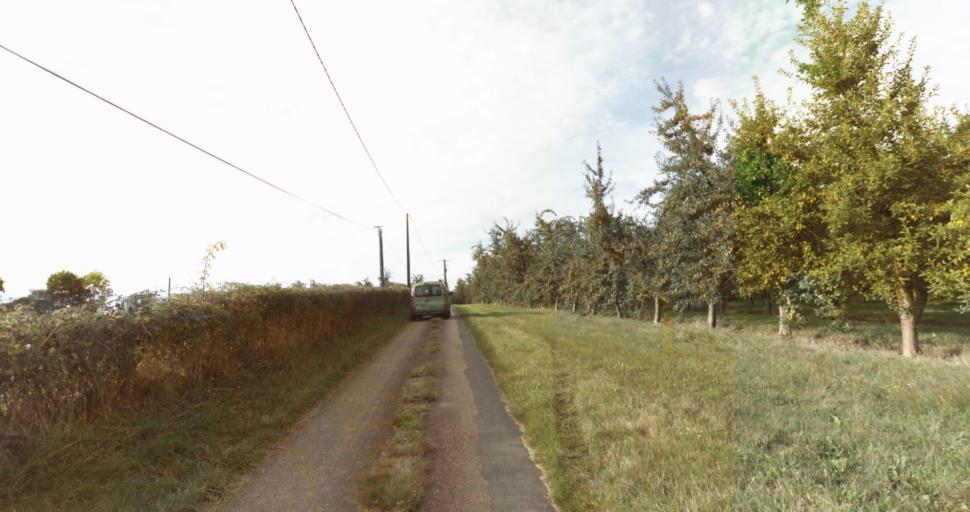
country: FR
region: Lower Normandy
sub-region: Departement de l'Orne
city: Gace
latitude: 48.6964
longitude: 0.3143
